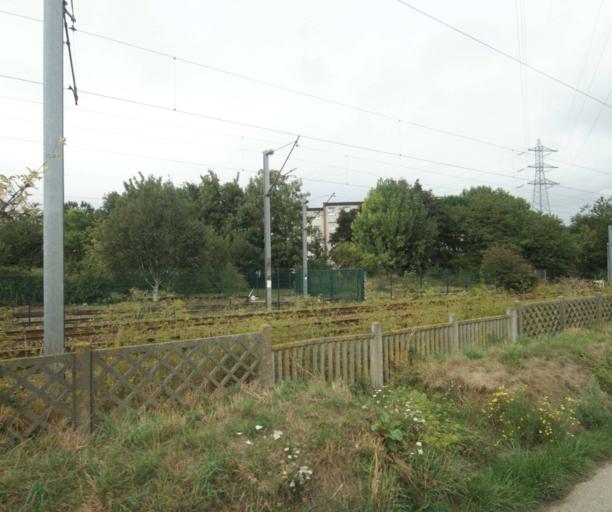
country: FR
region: Nord-Pas-de-Calais
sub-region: Departement du Nord
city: Lezennes
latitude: 50.6232
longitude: 3.1191
